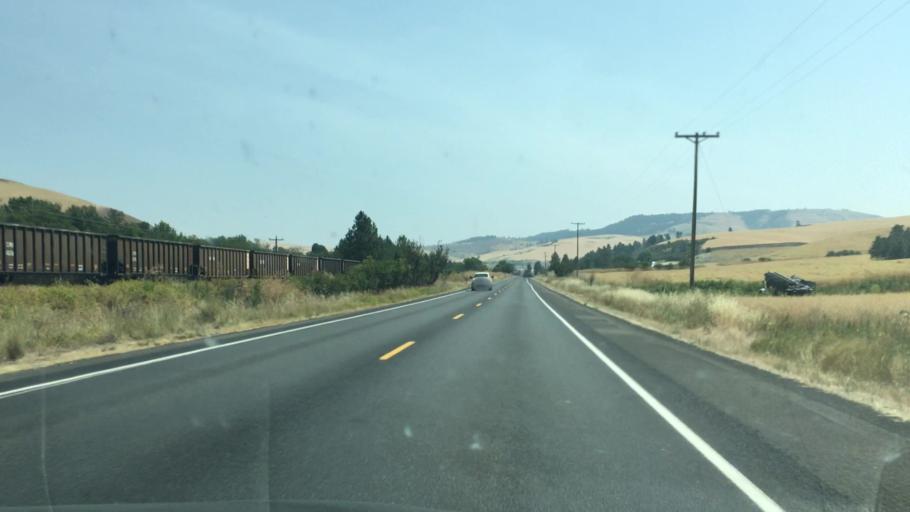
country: US
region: Idaho
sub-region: Nez Perce County
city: Lapwai
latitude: 46.3726
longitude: -116.6972
